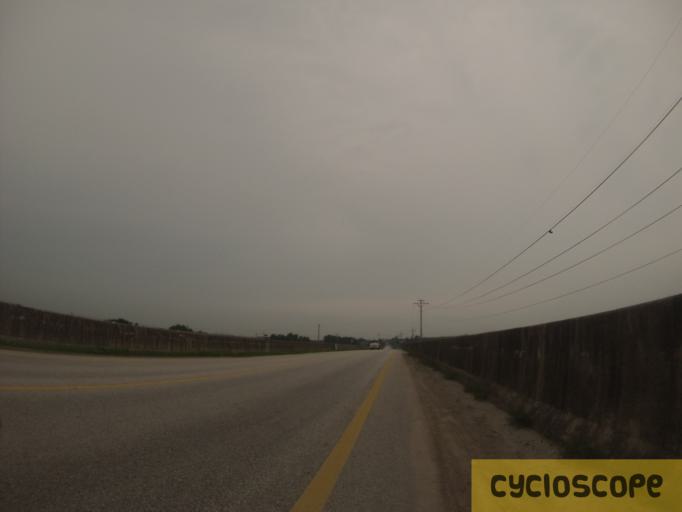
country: KR
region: Jeollabuk-do
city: Kimje
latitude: 35.8681
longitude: 126.8219
